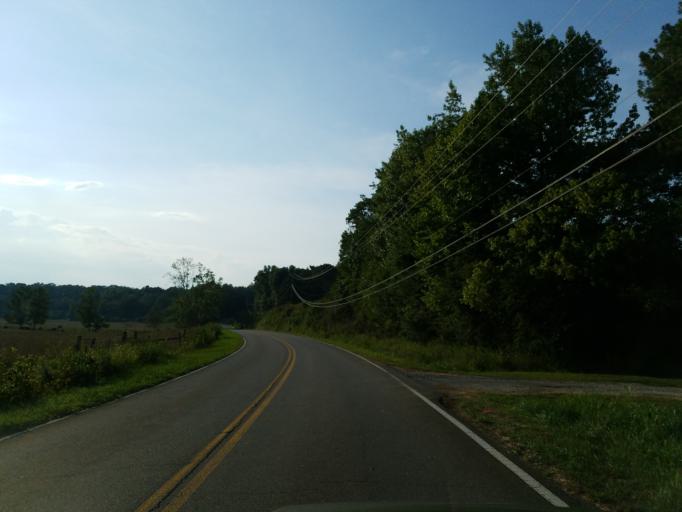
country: US
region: Georgia
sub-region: Pickens County
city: Jasper
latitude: 34.5250
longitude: -84.5248
